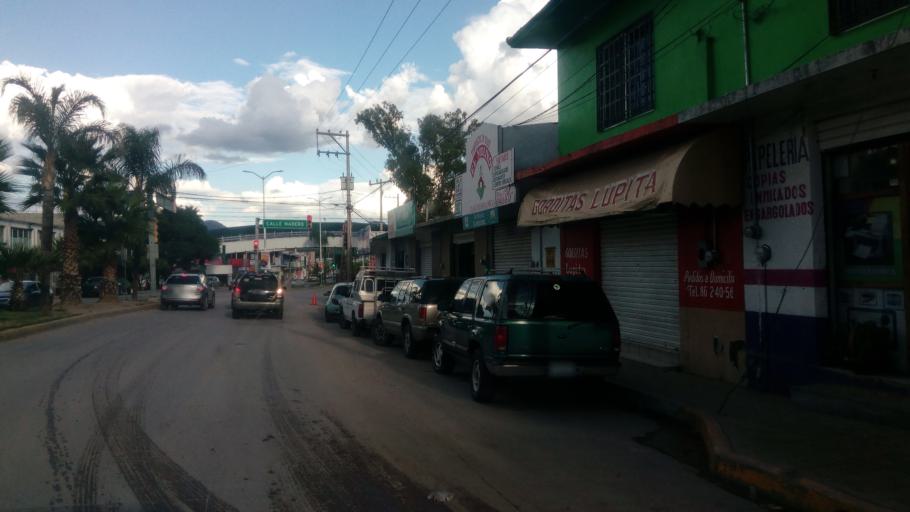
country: MX
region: Durango
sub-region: Santiago Papasquiaro
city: Santiago Papasquiaro
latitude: 25.0474
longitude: -105.4212
